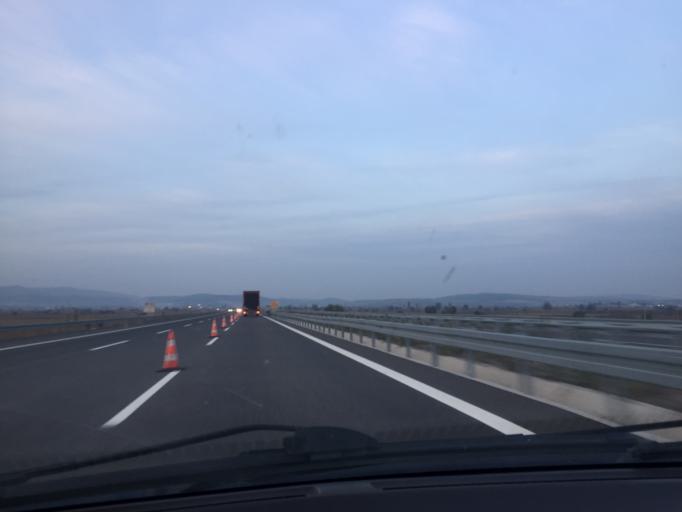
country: TR
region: Manisa
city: Halitpasa
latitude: 38.7413
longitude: 27.6584
